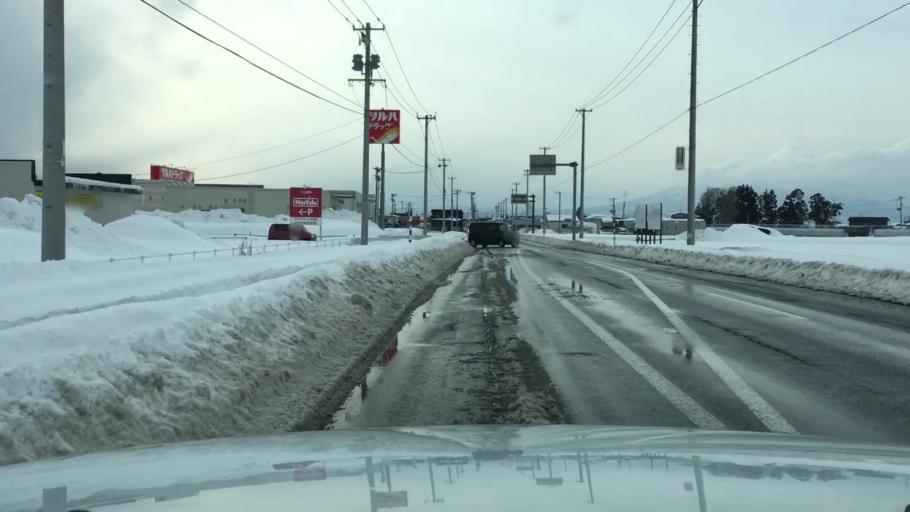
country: JP
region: Aomori
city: Kuroishi
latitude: 40.5918
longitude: 140.5684
